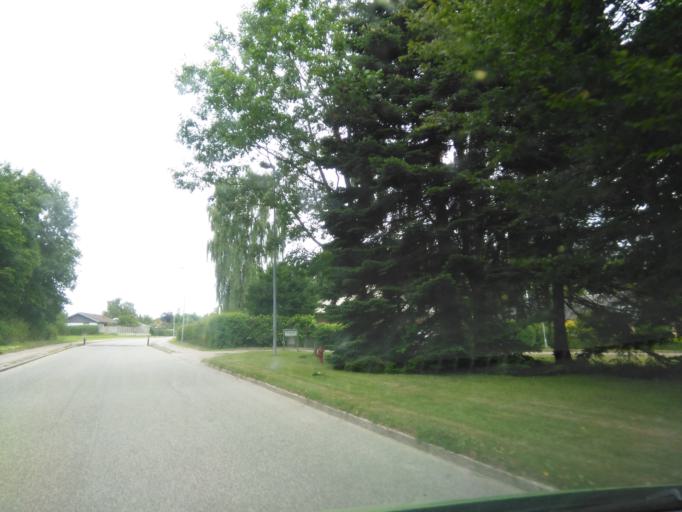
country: DK
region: Central Jutland
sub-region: Arhus Kommune
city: Marslet
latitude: 56.0637
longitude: 10.1653
